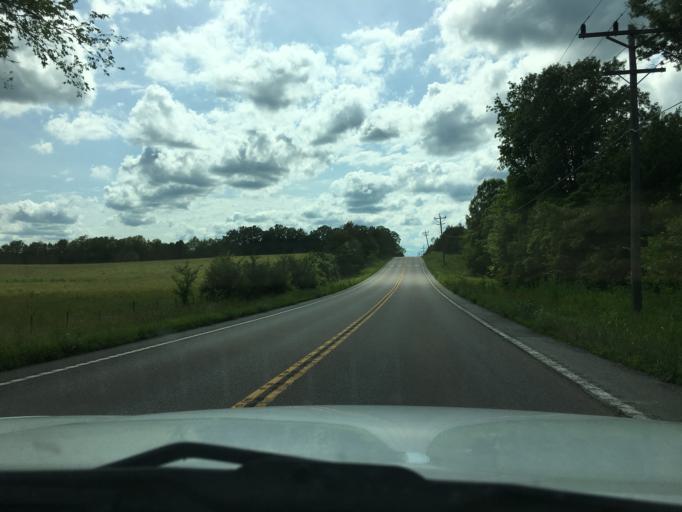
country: US
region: Missouri
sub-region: Franklin County
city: Gerald
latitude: 38.3875
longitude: -91.3824
